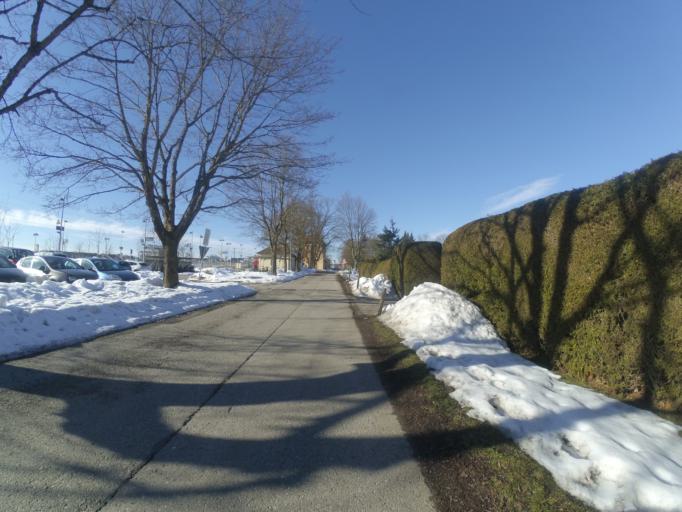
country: DE
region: Bavaria
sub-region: Upper Bavaria
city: Aying
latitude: 47.9684
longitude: 11.7706
